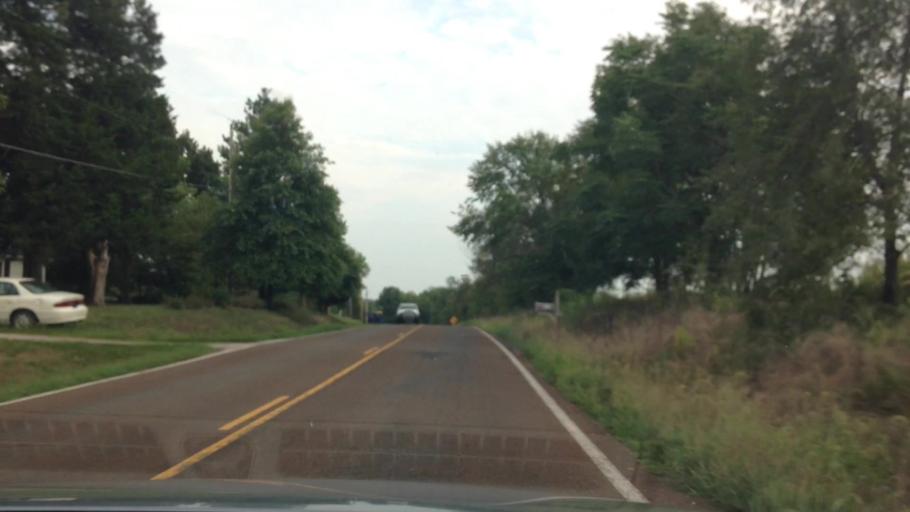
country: US
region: Missouri
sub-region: Clay County
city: Smithville
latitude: 39.4008
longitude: -94.5890
